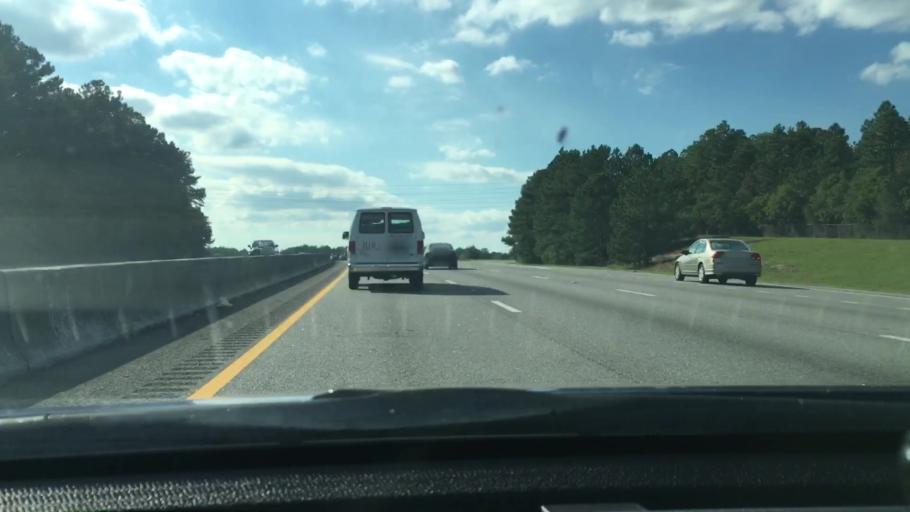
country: US
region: South Carolina
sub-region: Richland County
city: Dentsville
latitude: 34.0740
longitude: -80.9632
